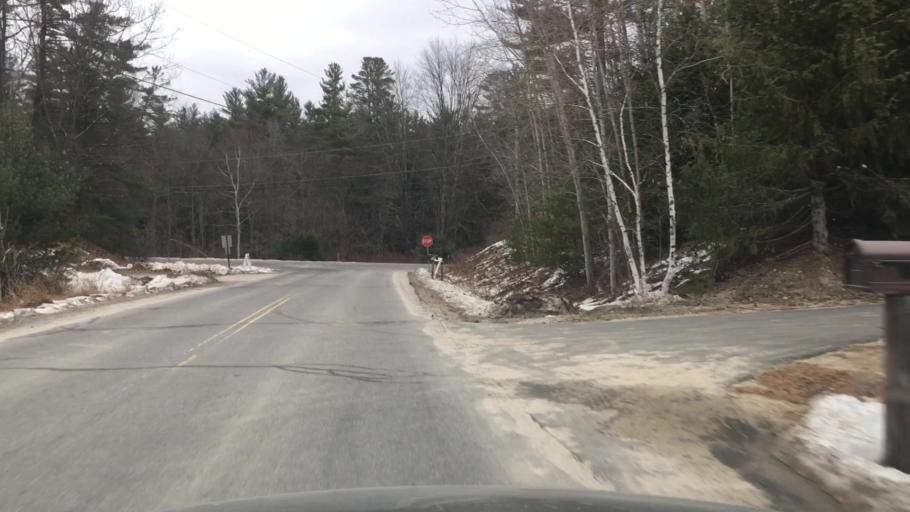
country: US
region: New Hampshire
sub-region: Hillsborough County
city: New Boston
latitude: 43.0002
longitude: -71.6617
